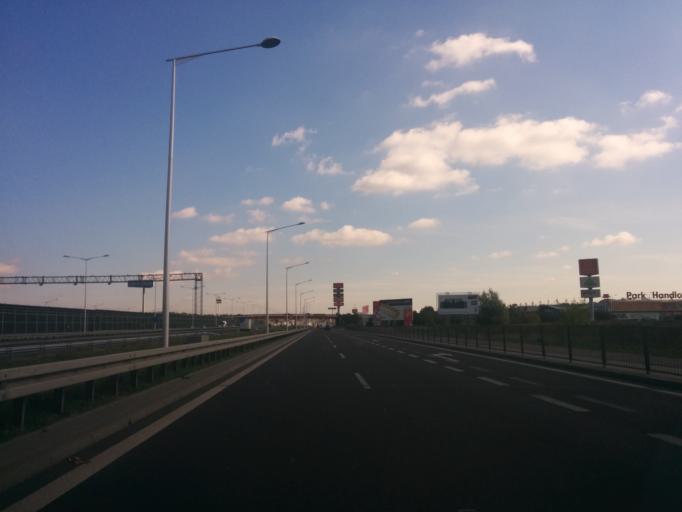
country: PL
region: Masovian Voivodeship
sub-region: Warszawa
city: Targowek
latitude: 52.3071
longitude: 21.0728
